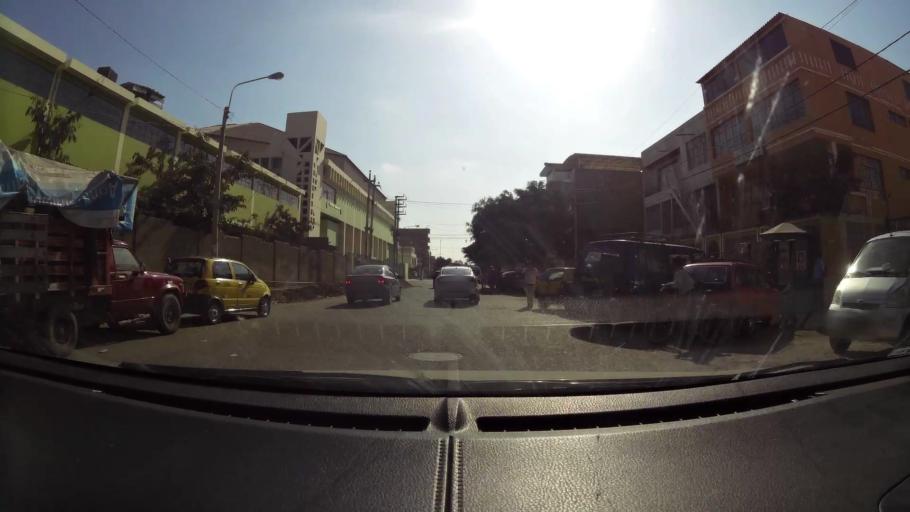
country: PE
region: Lambayeque
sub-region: Provincia de Chiclayo
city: Chiclayo
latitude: -6.7647
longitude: -79.8421
